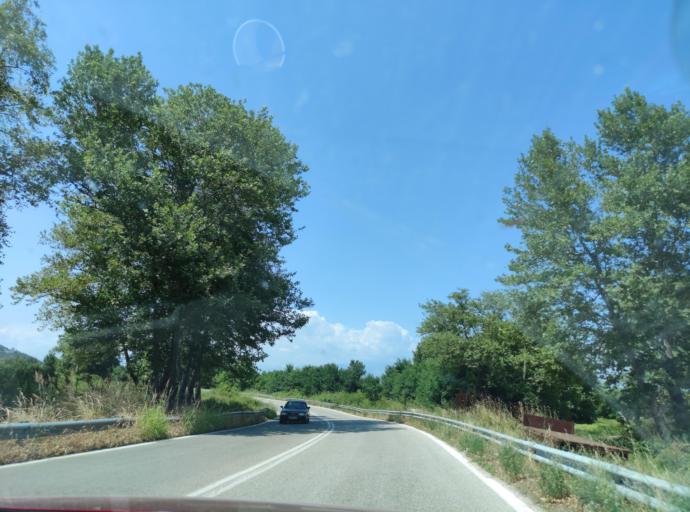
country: GR
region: East Macedonia and Thrace
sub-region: Nomos Kavalas
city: Palaiochori
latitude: 40.9559
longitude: 24.1933
